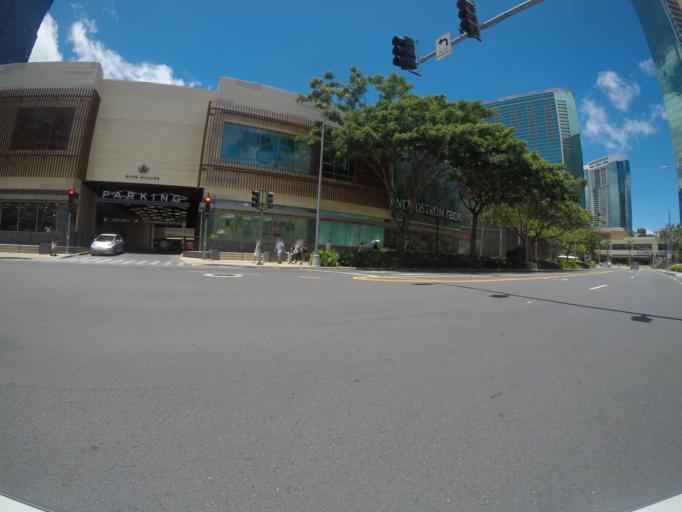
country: US
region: Hawaii
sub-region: Honolulu County
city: Honolulu
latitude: 21.2929
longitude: -157.8516
